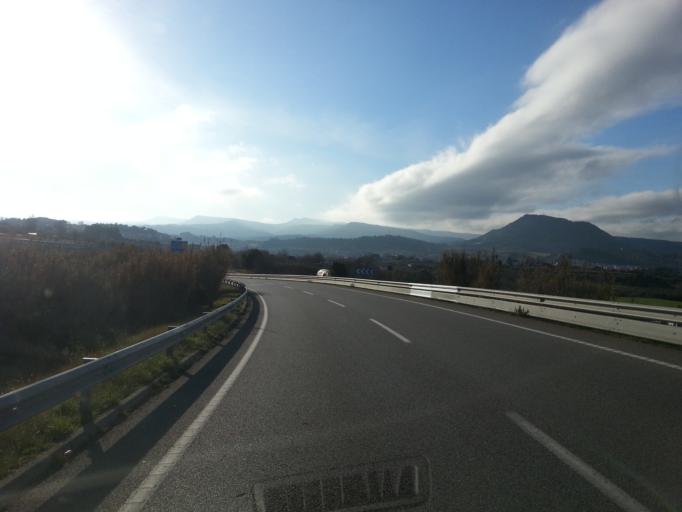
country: ES
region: Catalonia
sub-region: Provincia de Barcelona
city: Manresa
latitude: 41.7450
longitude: 1.8296
